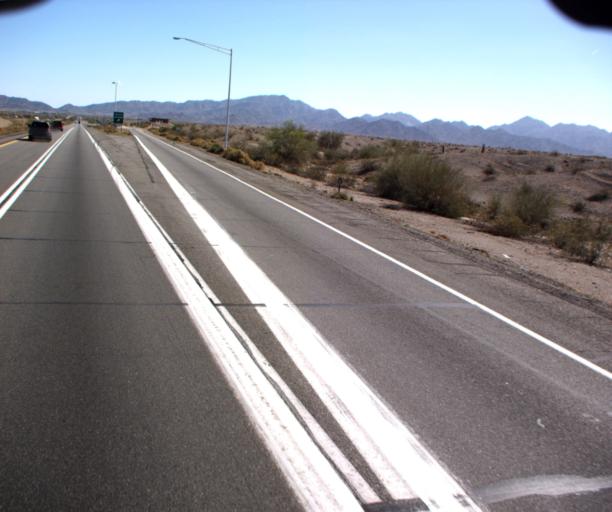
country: US
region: Arizona
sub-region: La Paz County
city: Ehrenberg
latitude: 33.6113
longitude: -114.4785
